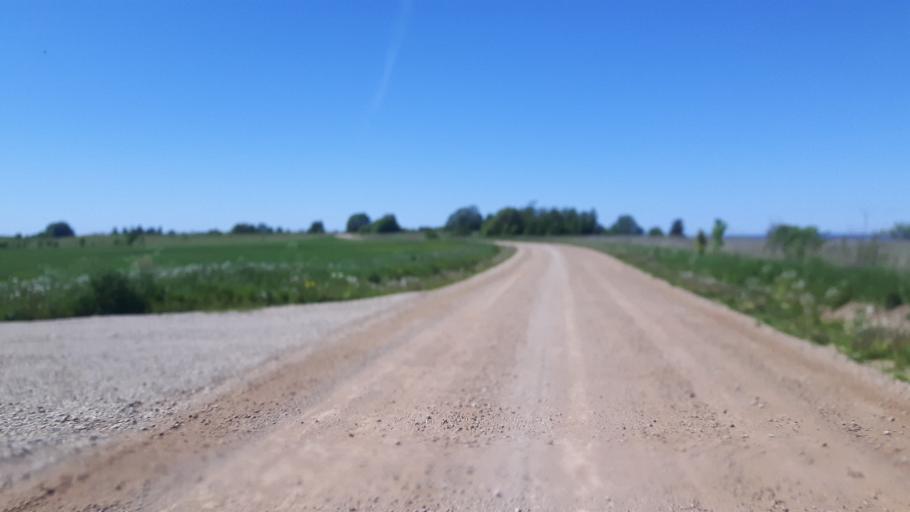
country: EE
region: Ida-Virumaa
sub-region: Toila vald
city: Voka
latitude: 59.4137
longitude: 27.6322
